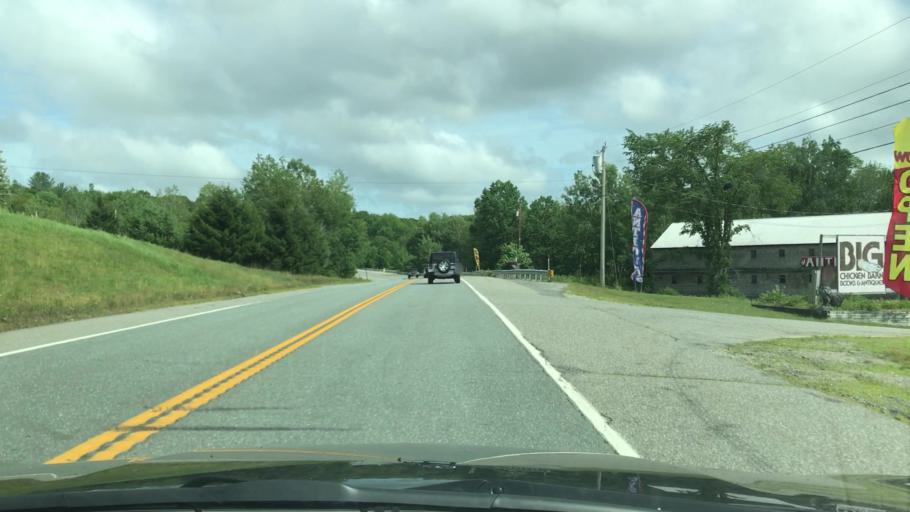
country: US
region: Maine
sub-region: Hancock County
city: Surry
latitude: 44.5625
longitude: -68.5874
